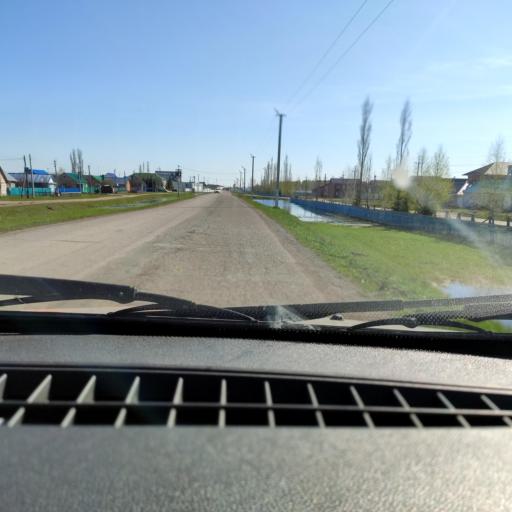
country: RU
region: Bashkortostan
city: Kabakovo
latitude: 54.6018
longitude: 56.1844
